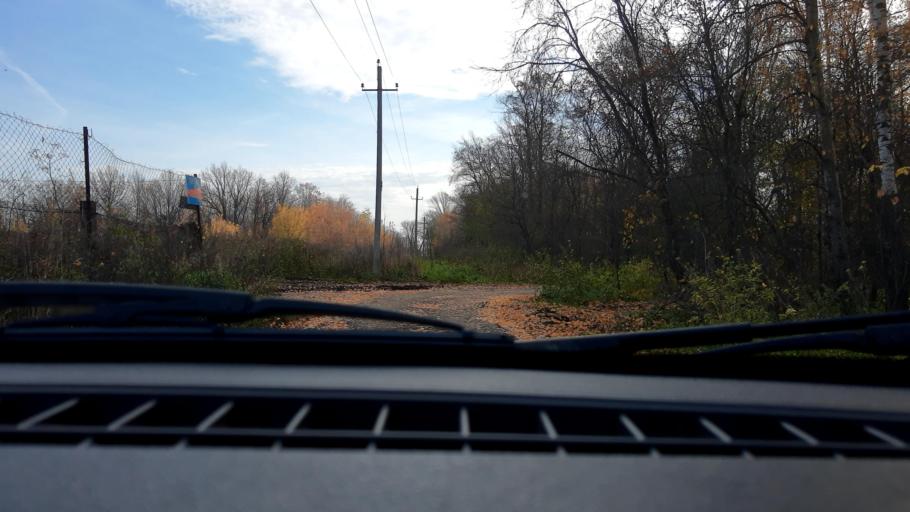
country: RU
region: Bashkortostan
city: Mikhaylovka
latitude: 54.8084
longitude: 55.8339
